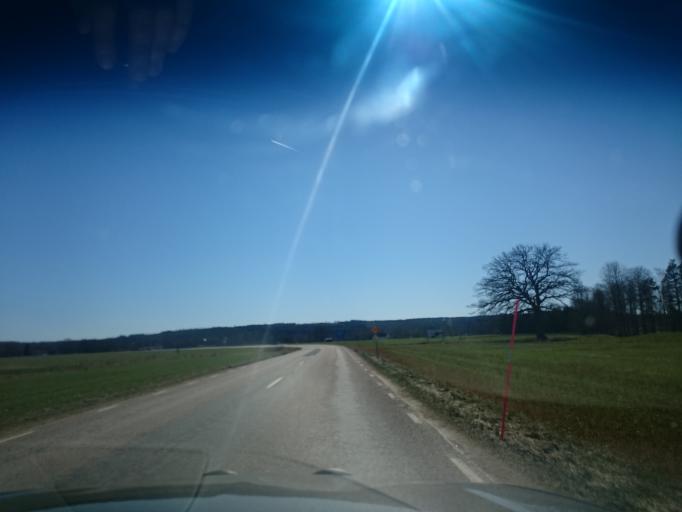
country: SE
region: Joenkoeping
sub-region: Vetlanda Kommun
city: Landsbro
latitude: 57.2103
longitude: 14.9439
